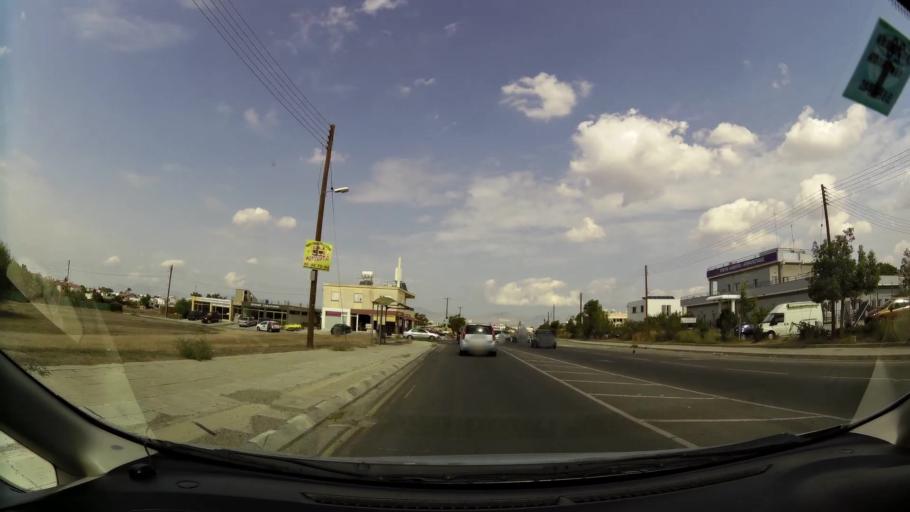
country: CY
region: Lefkosia
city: Tseri
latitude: 35.1155
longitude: 33.3326
